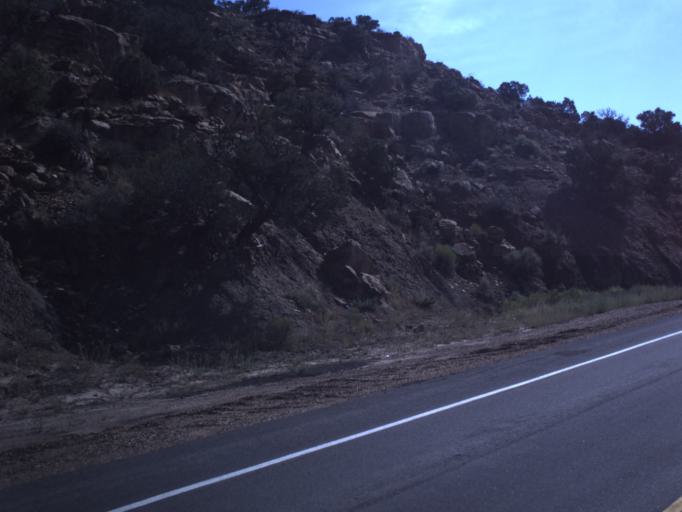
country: US
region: Utah
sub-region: Duchesne County
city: Duchesne
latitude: 40.3589
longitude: -110.3949
